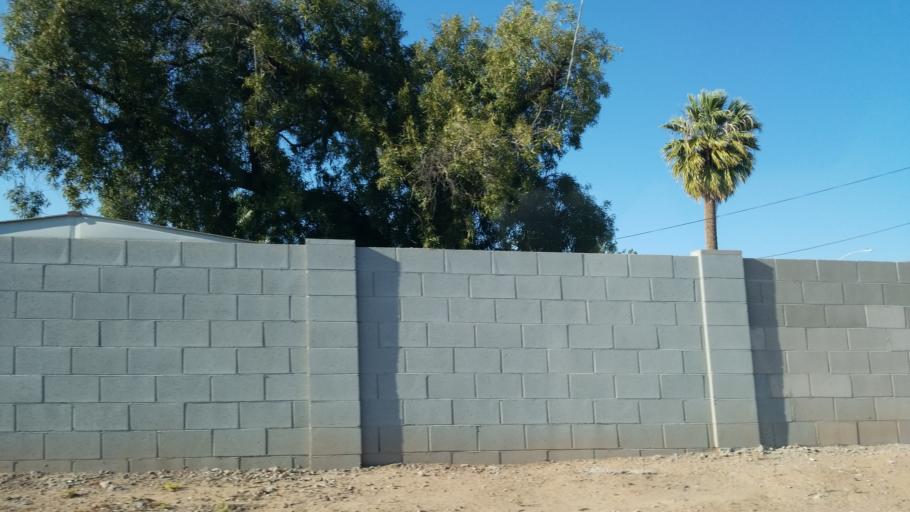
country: US
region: Arizona
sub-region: Maricopa County
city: Glendale
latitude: 33.5294
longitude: -112.1648
